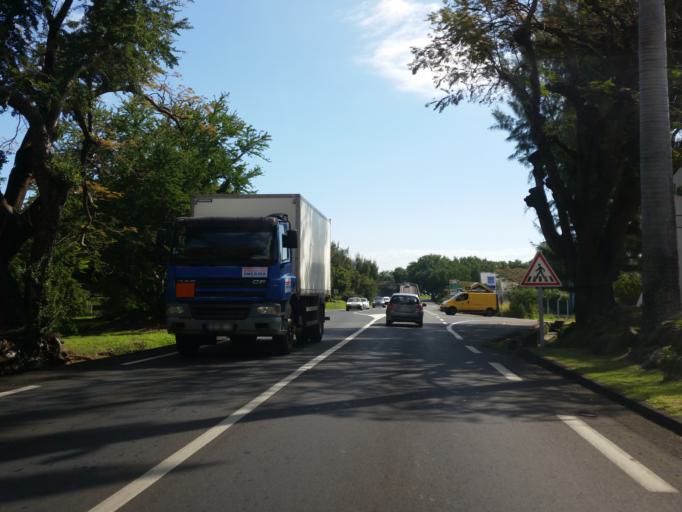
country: RE
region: Reunion
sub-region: Reunion
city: Saint-Denis
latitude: -20.8898
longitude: 55.4905
